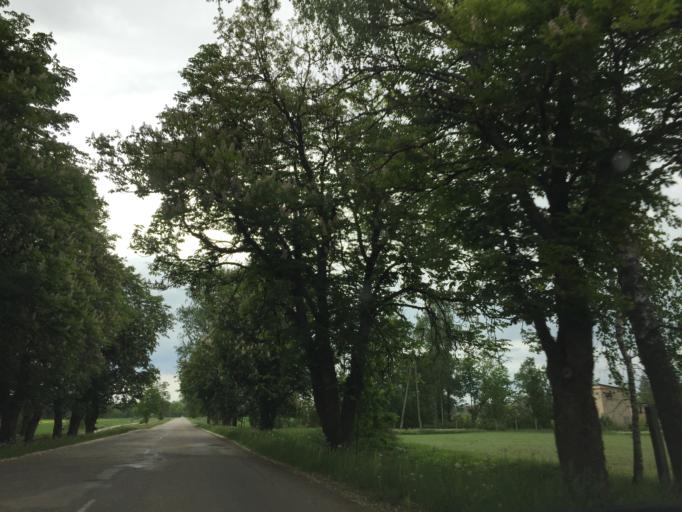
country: LV
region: Preilu Rajons
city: Preili
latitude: 56.0674
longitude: 26.7561
